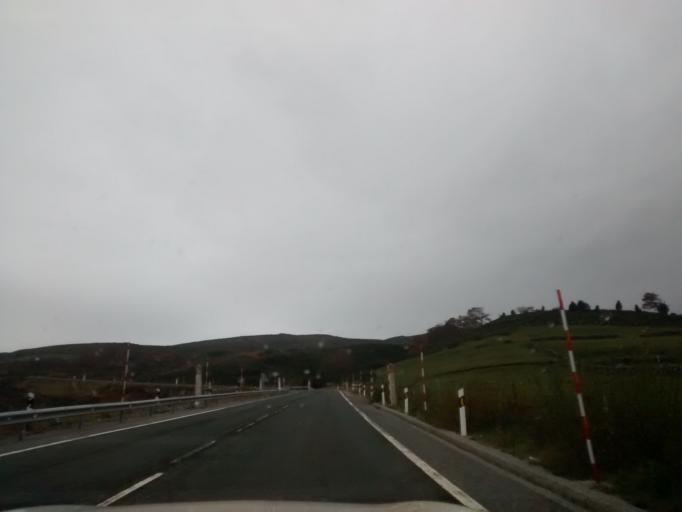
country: ES
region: Cantabria
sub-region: Provincia de Cantabria
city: San Pedro del Romeral
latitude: 43.0632
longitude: -3.8853
